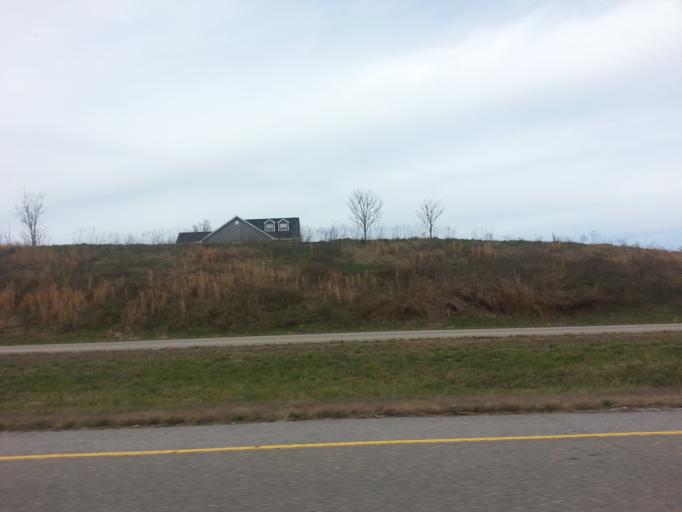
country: US
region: Tennessee
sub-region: Cocke County
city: Newport
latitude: 36.0139
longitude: -83.0525
